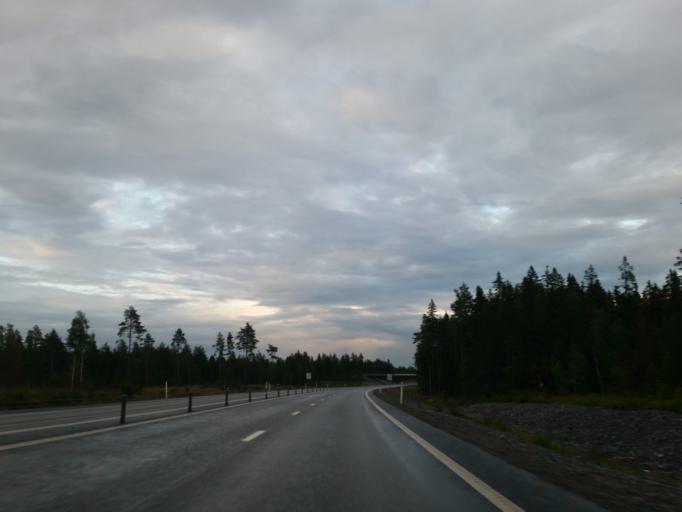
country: SE
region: Vaesterbotten
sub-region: Umea Kommun
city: Umea
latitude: 63.8584
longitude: 20.2279
